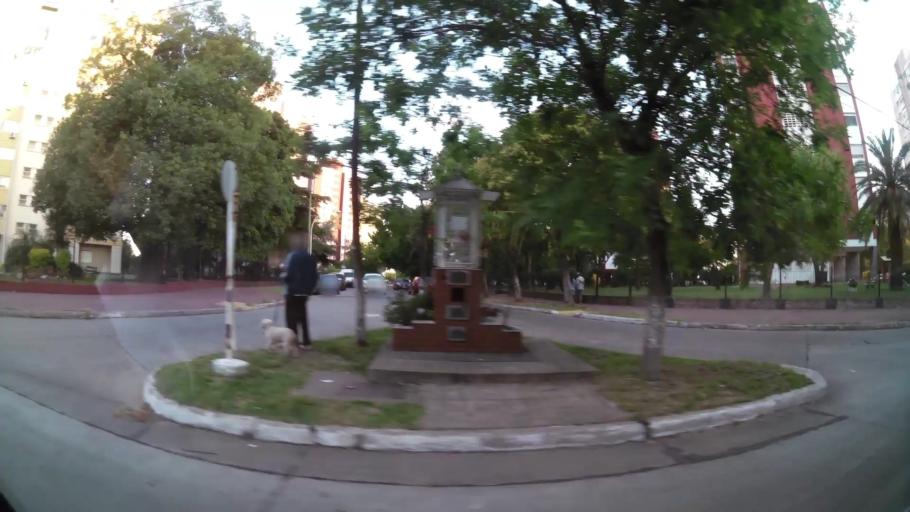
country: AR
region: Buenos Aires F.D.
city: Villa Lugano
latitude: -34.6952
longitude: -58.4762
